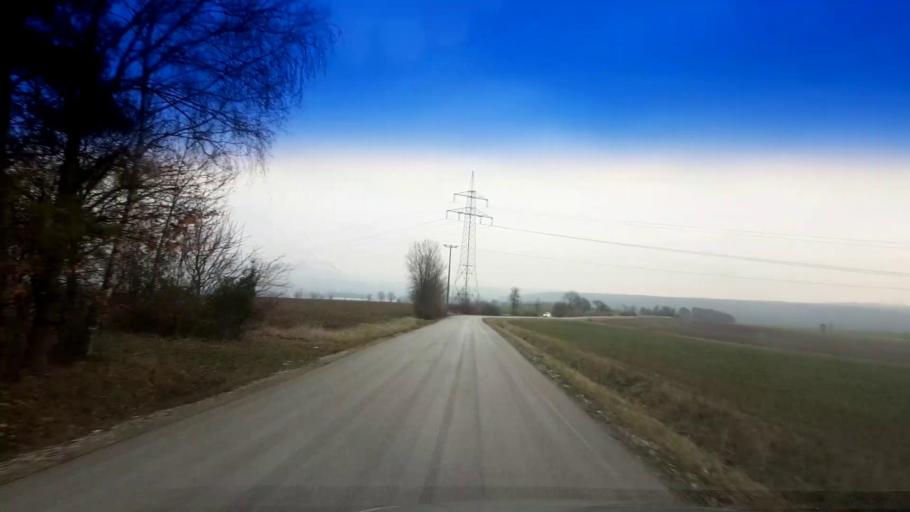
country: DE
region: Bavaria
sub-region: Upper Franconia
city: Hallerndorf
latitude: 49.7788
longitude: 10.9811
